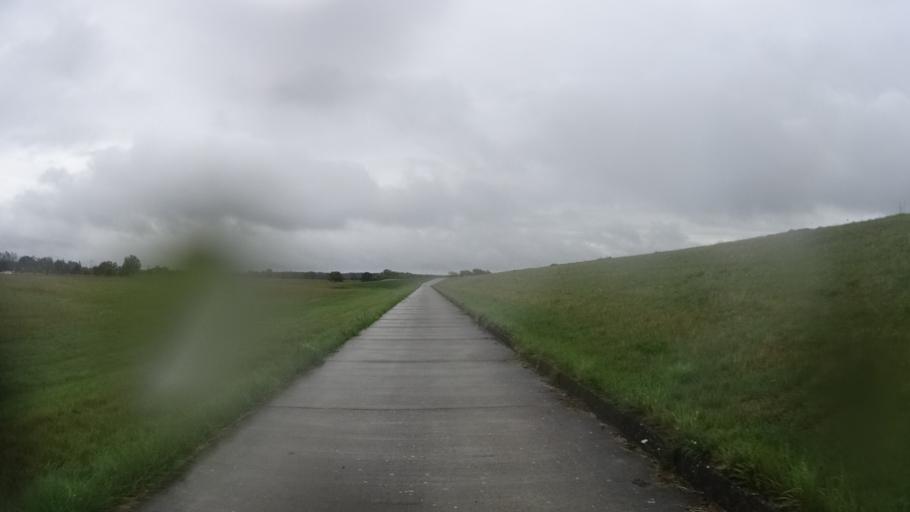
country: DE
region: Lower Saxony
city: Damnatz
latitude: 53.1767
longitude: 11.1477
